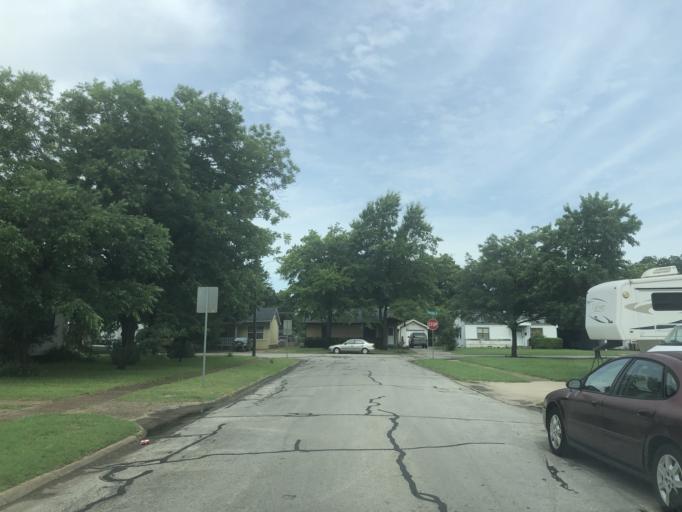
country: US
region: Texas
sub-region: Dallas County
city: Irving
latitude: 32.8020
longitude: -96.9512
